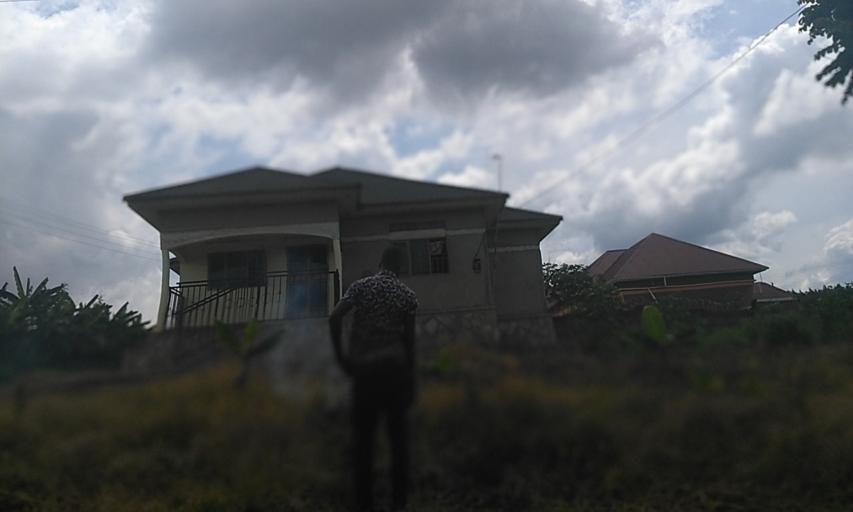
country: UG
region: Central Region
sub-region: Wakiso District
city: Wakiso
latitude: 0.3550
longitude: 32.4620
